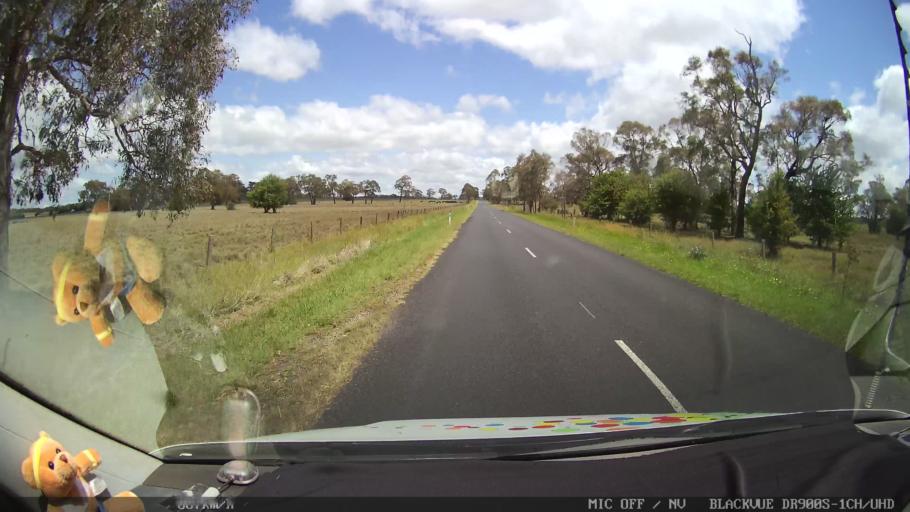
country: AU
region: New South Wales
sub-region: Glen Innes Severn
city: Glen Innes
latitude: -29.6278
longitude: 151.6731
